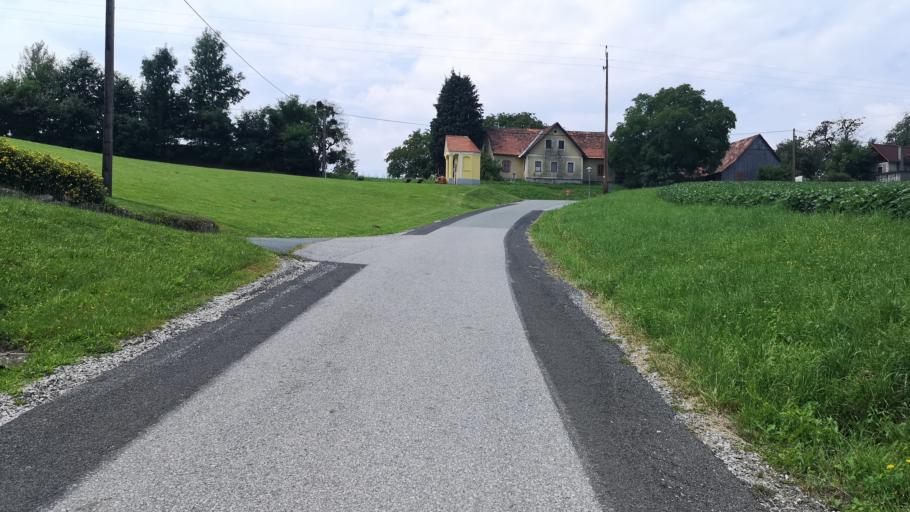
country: AT
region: Styria
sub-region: Politischer Bezirk Leibnitz
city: Weitendorf
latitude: 46.8736
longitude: 15.4580
